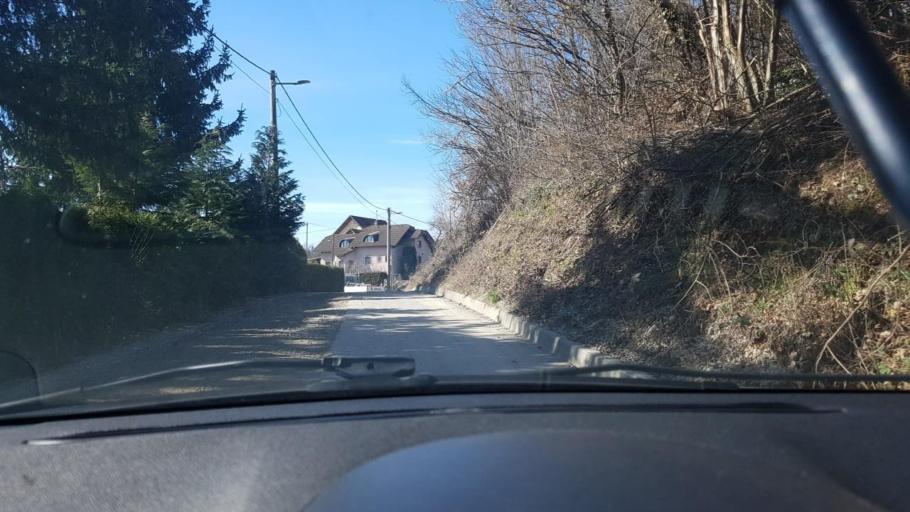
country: HR
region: Zagrebacka
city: Pojatno
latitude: 45.9080
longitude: 15.8039
